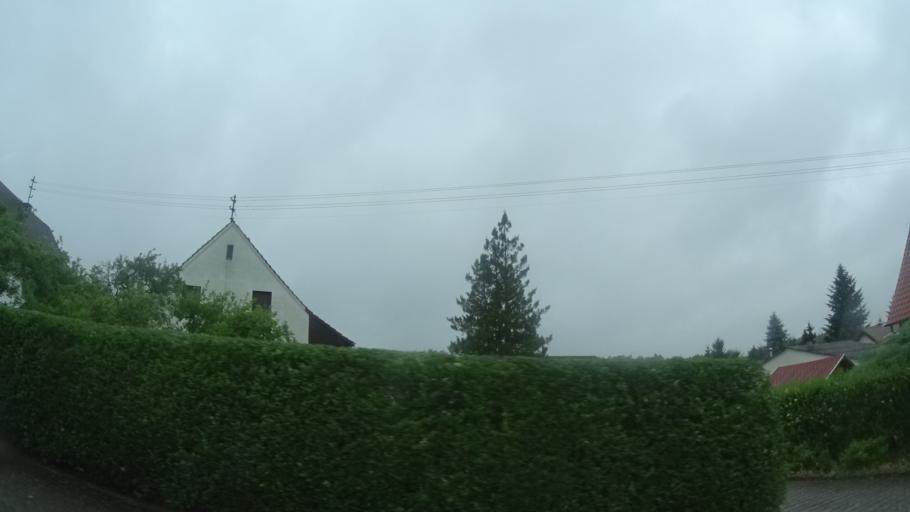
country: DE
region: Rheinland-Pfalz
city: Gries
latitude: 49.4173
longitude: 7.4268
